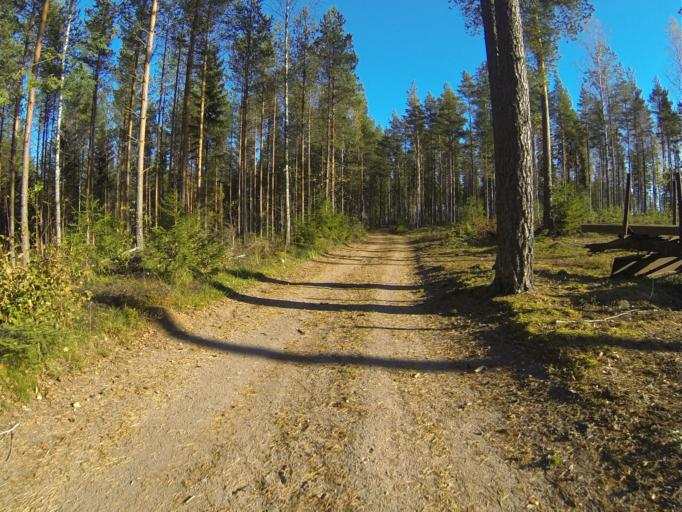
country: FI
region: Varsinais-Suomi
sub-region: Salo
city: Saerkisalo
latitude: 60.2144
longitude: 22.9814
